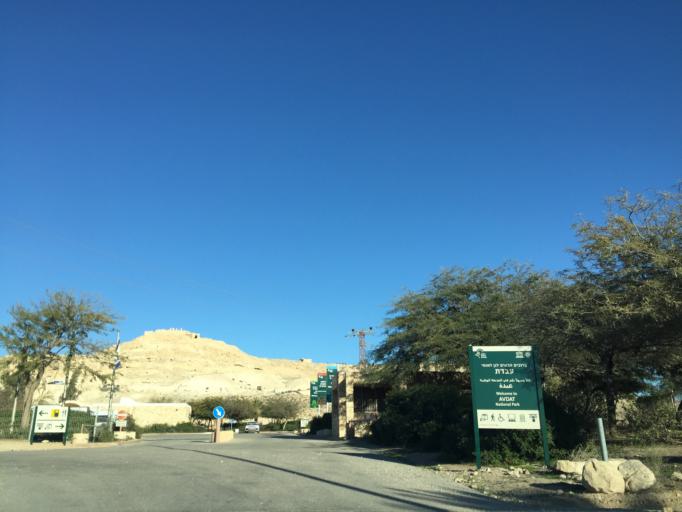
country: IL
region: Southern District
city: Midreshet Ben-Gurion
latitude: 30.7917
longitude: 34.7683
